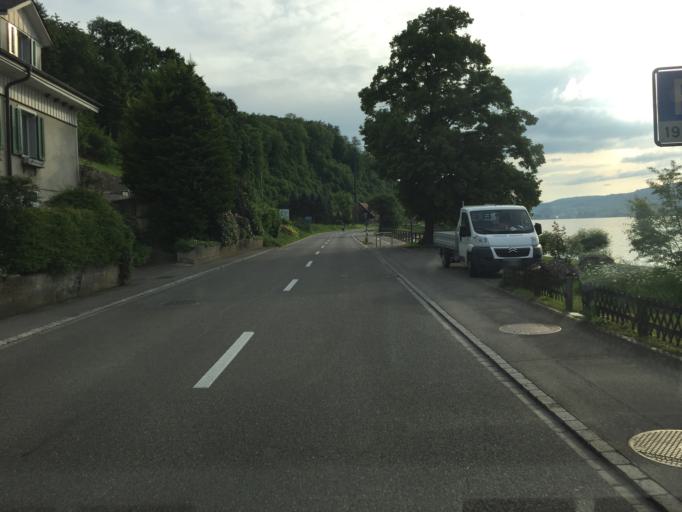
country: CH
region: Thurgau
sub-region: Frauenfeld District
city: Steckborn
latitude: 47.6727
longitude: 9.0141
